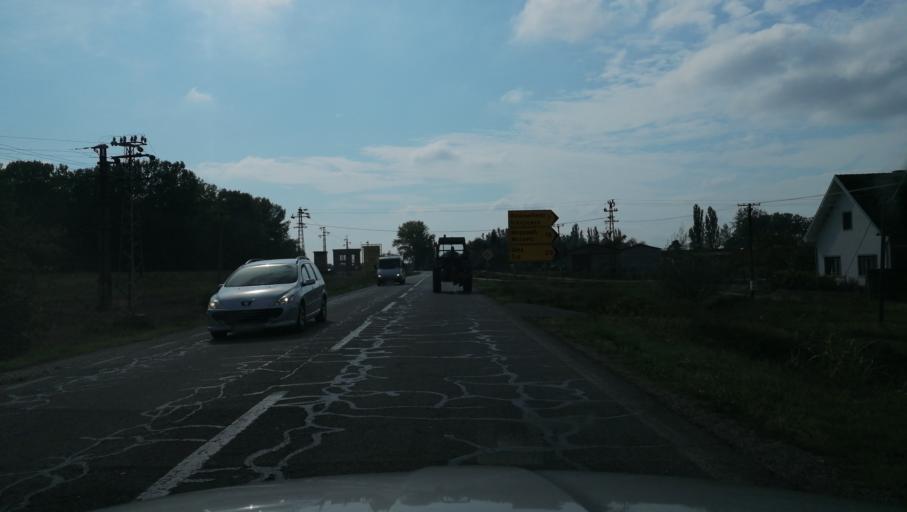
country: RS
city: Bosut
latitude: 44.9467
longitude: 19.3694
